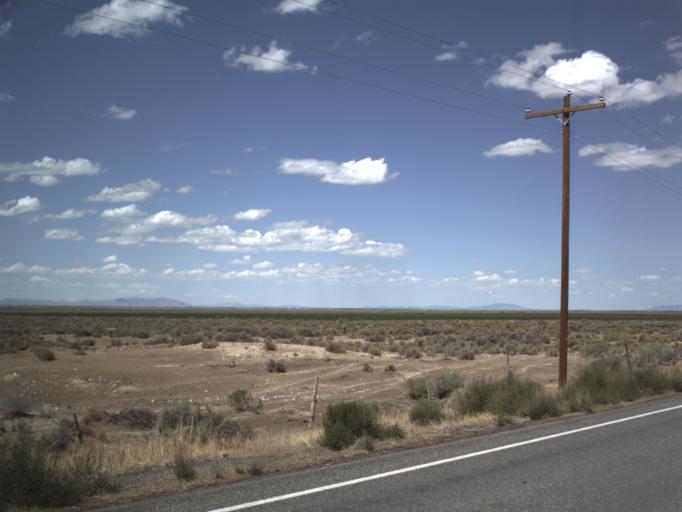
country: US
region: Utah
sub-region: Millard County
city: Fillmore
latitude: 39.1769
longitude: -112.4100
